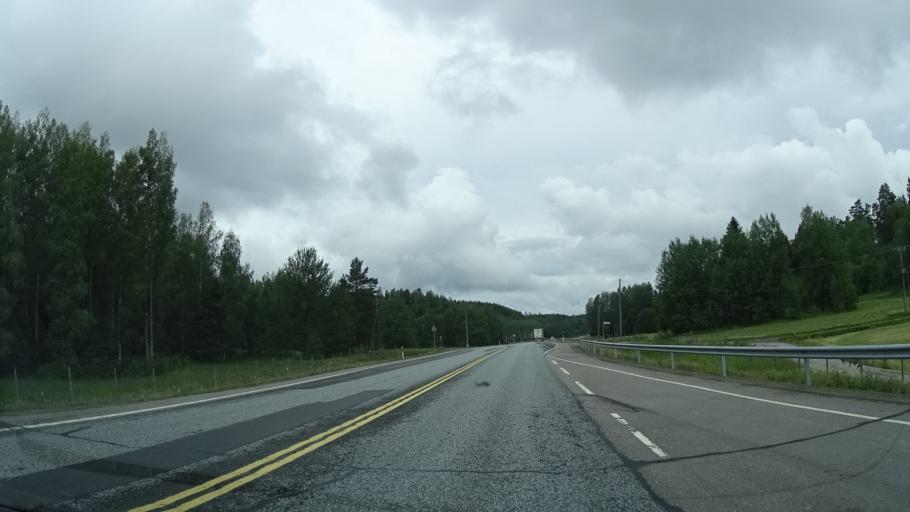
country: FI
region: Uusimaa
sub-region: Helsinki
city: Karkkila
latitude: 60.5771
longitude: 24.1397
